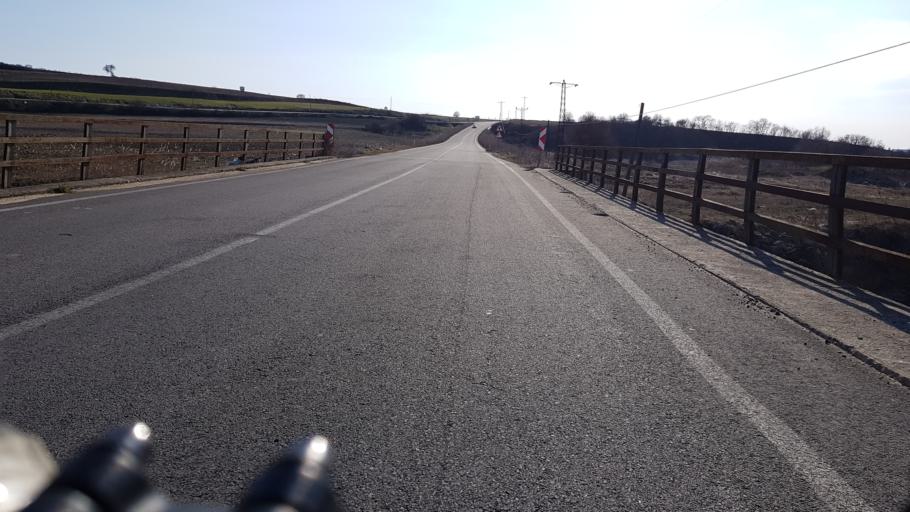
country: TR
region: Tekirdag
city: Velimese
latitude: 41.3576
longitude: 27.8511
